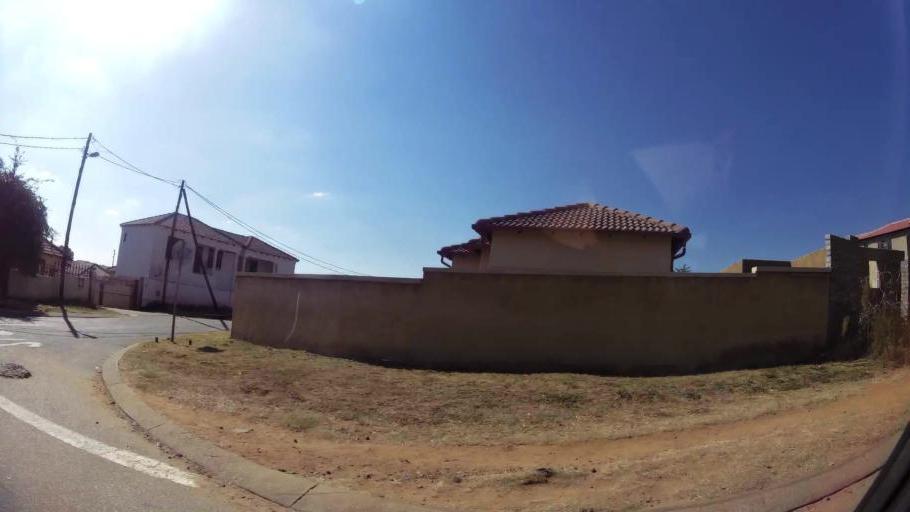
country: ZA
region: Gauteng
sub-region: West Rand District Municipality
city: Muldersdriseloop
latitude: -26.0221
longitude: 27.9355
